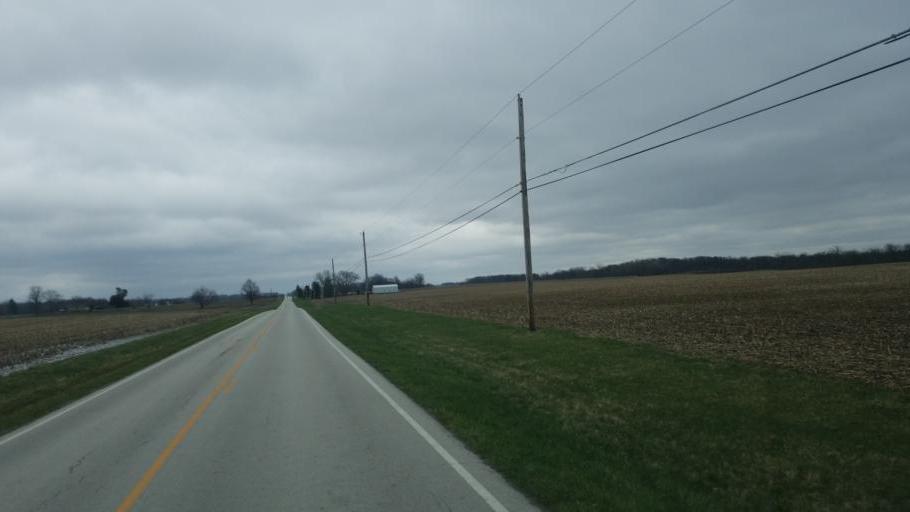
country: US
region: Ohio
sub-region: Wyandot County
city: Upper Sandusky
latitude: 40.8258
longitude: -83.2196
